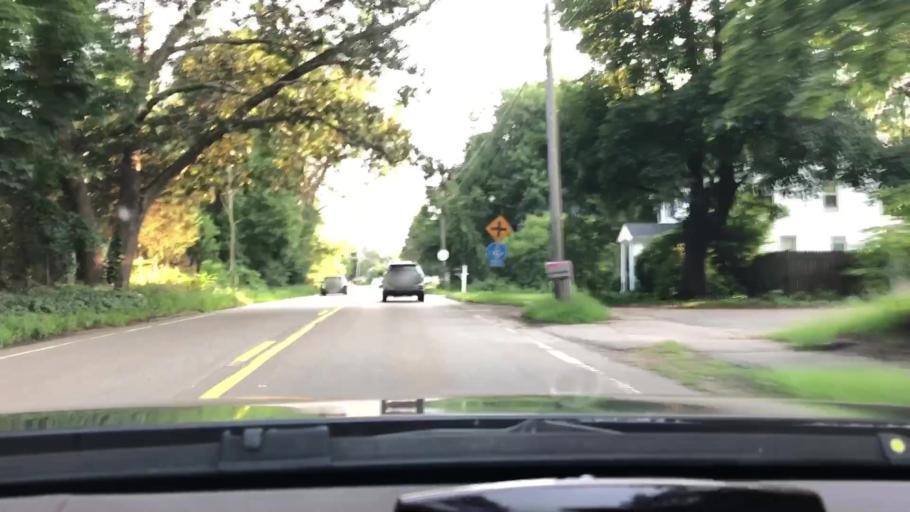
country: US
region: Massachusetts
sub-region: Norfolk County
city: Walpole
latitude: 42.1698
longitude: -71.2275
